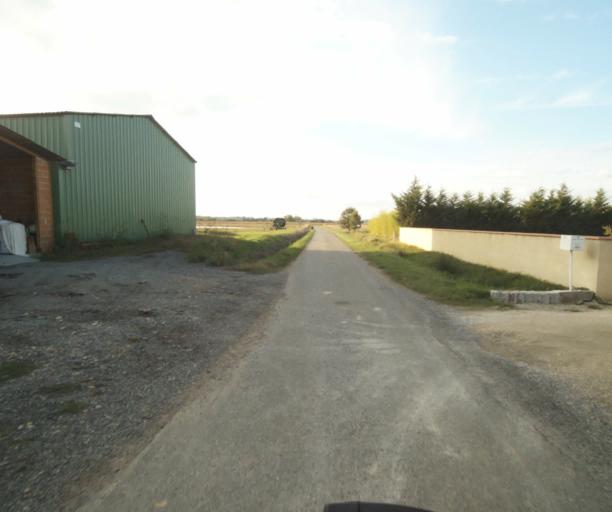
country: FR
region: Midi-Pyrenees
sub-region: Departement du Tarn-et-Garonne
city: Verdun-sur-Garonne
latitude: 43.8236
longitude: 1.1575
